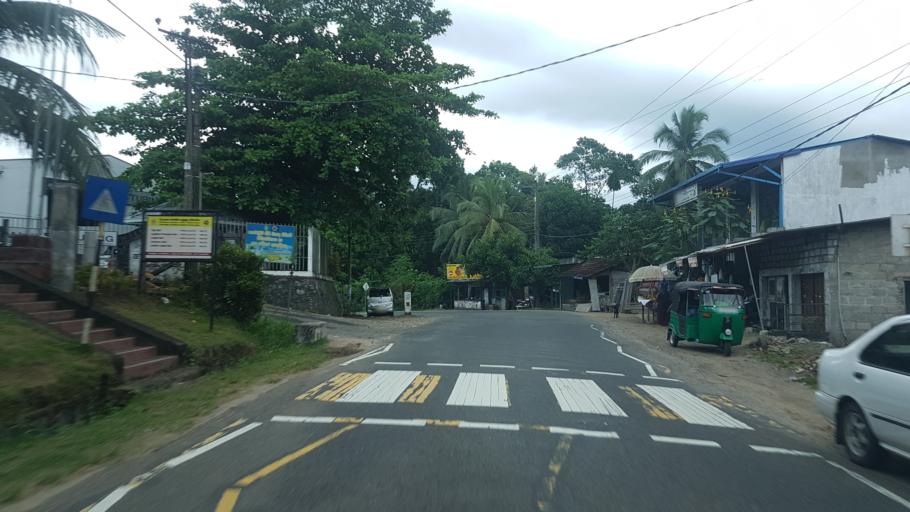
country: LK
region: Western
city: Hanwella Ihala
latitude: 7.0302
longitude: 80.2832
